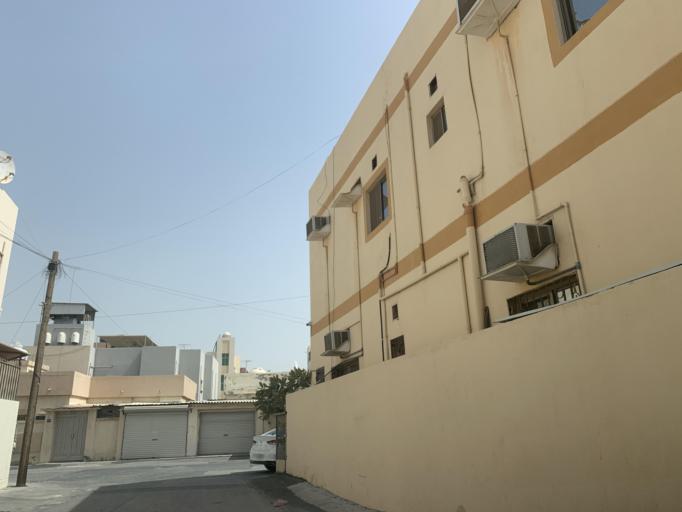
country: BH
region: Northern
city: Madinat `Isa
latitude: 26.1756
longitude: 50.5578
